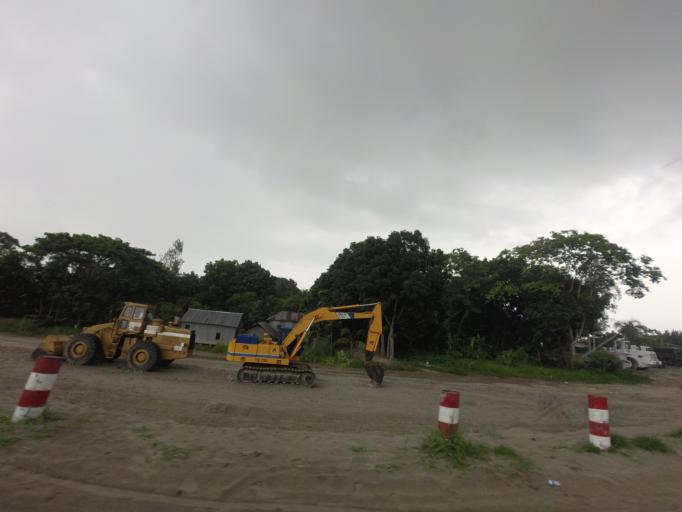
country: BD
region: Dhaka
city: Char Bhadrasan
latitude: 23.3776
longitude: 90.1063
